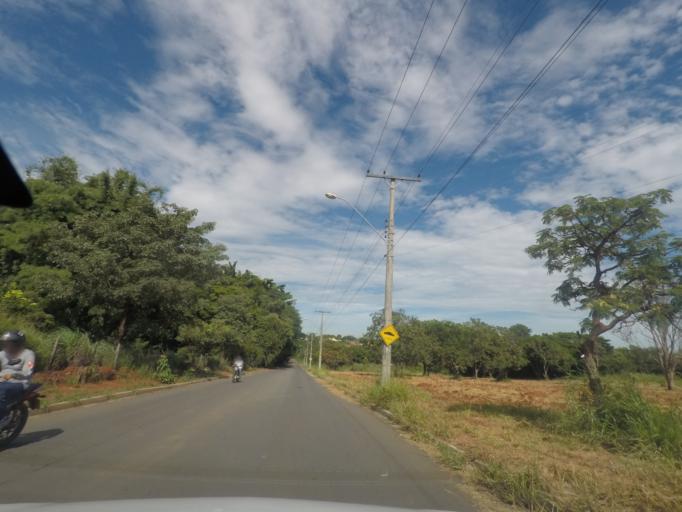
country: BR
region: Goias
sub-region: Aparecida De Goiania
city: Aparecida de Goiania
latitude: -16.7980
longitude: -49.2710
